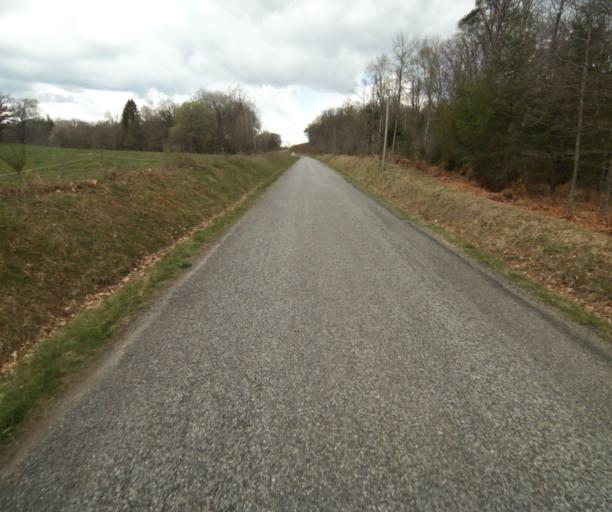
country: FR
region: Limousin
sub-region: Departement de la Correze
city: Correze
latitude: 45.2635
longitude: 1.9051
